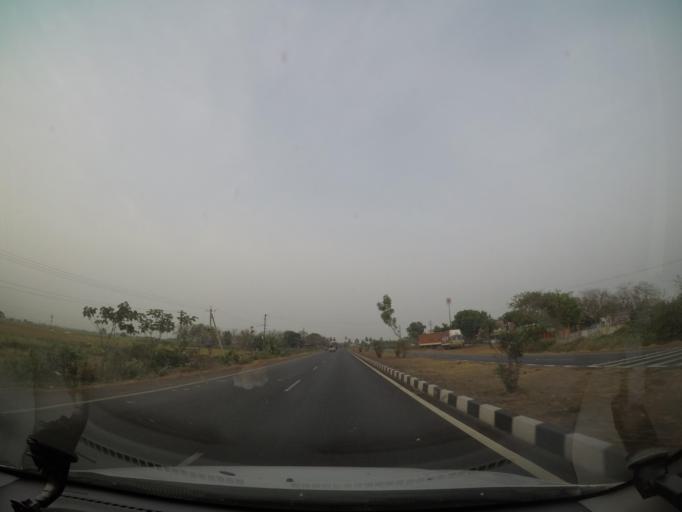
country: IN
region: Andhra Pradesh
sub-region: Krishna
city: Gannavaram
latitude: 16.6134
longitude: 80.9234
